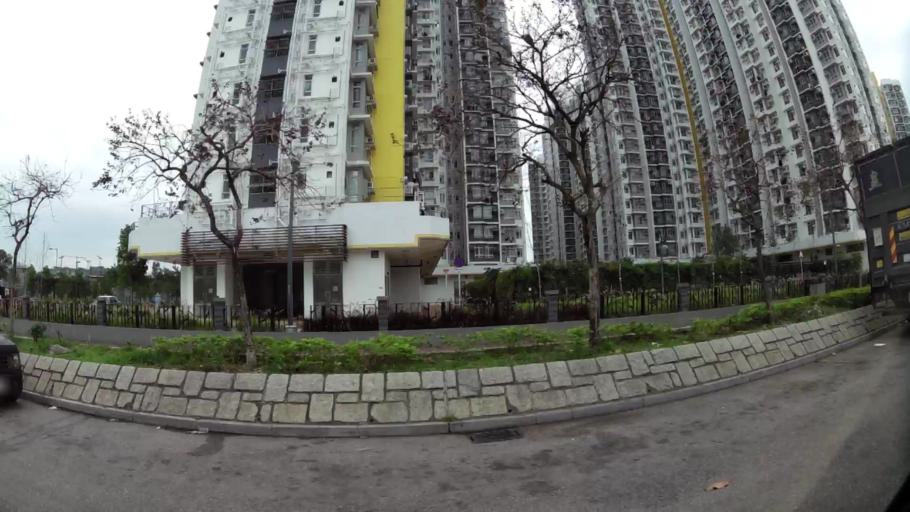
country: HK
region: Yuen Long
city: Yuen Long Kau Hui
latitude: 22.4385
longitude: 113.9963
